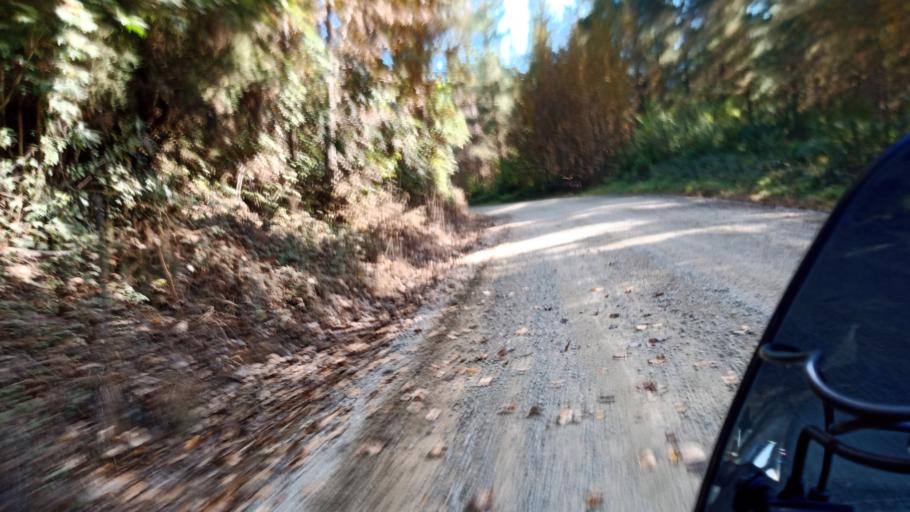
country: NZ
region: Hawke's Bay
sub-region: Wairoa District
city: Wairoa
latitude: -38.9288
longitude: 177.2177
